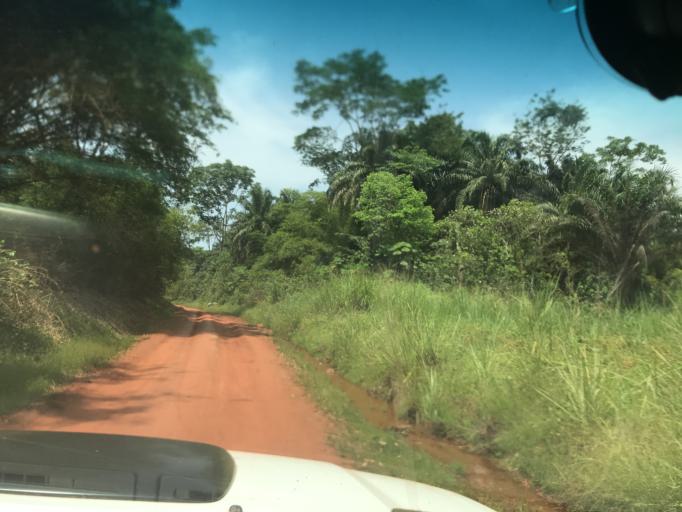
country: CD
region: Eastern Province
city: Aketi
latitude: 2.8878
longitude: 23.9784
